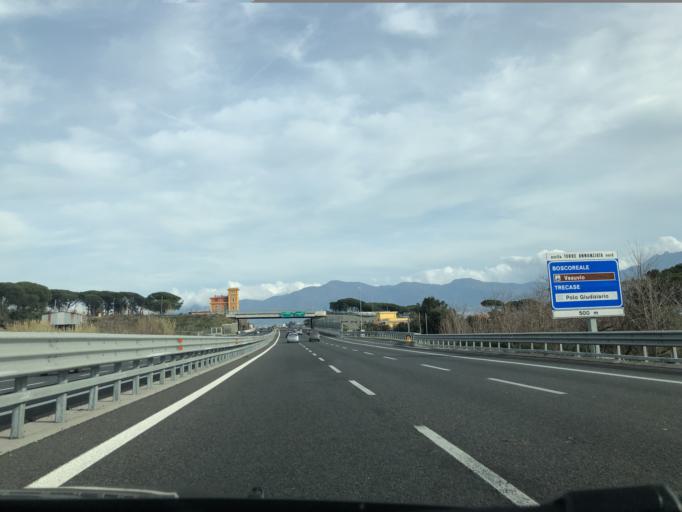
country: IT
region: Campania
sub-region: Provincia di Napoli
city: Trecase
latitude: 40.7706
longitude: 14.4174
